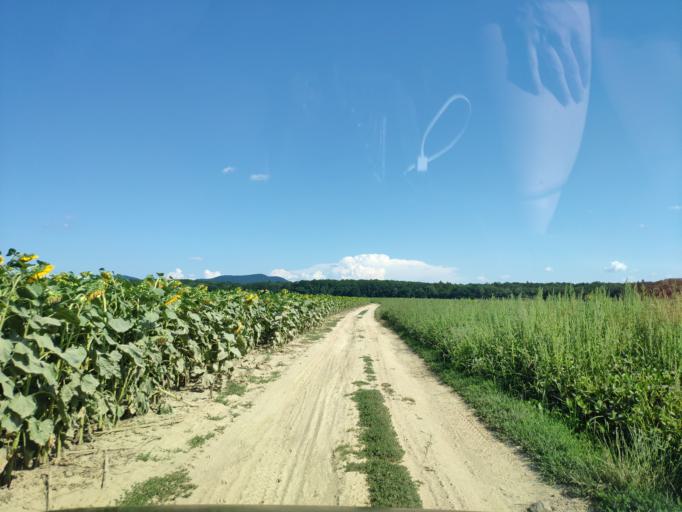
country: SK
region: Presovsky
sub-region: Okres Presov
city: Presov
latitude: 48.9068
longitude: 21.2746
